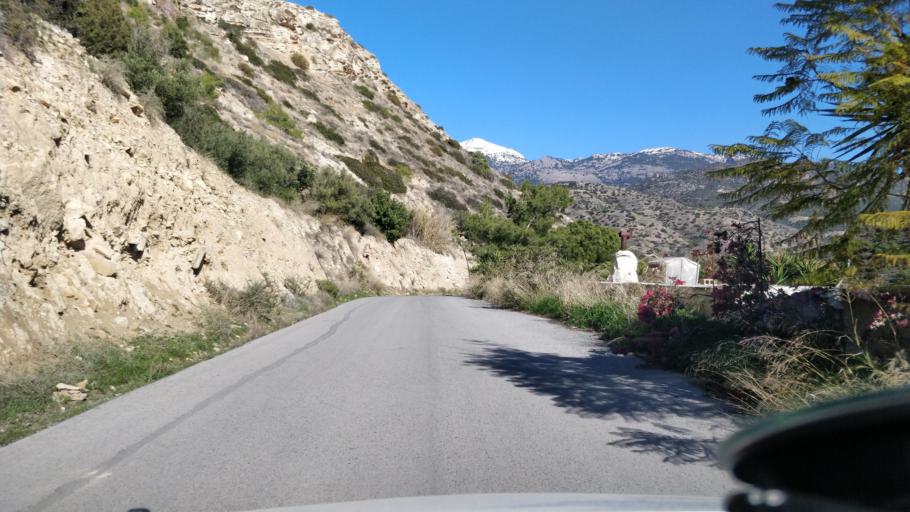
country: GR
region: Crete
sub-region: Nomos Lasithiou
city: Gra Liyia
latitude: 34.9891
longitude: 25.4815
